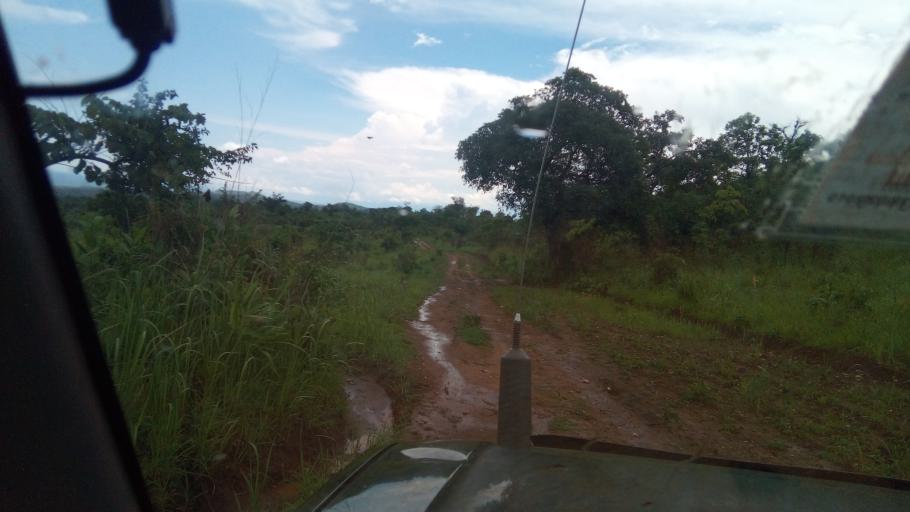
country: CD
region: Katanga
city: Kalemie
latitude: -5.7090
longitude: 29.3013
